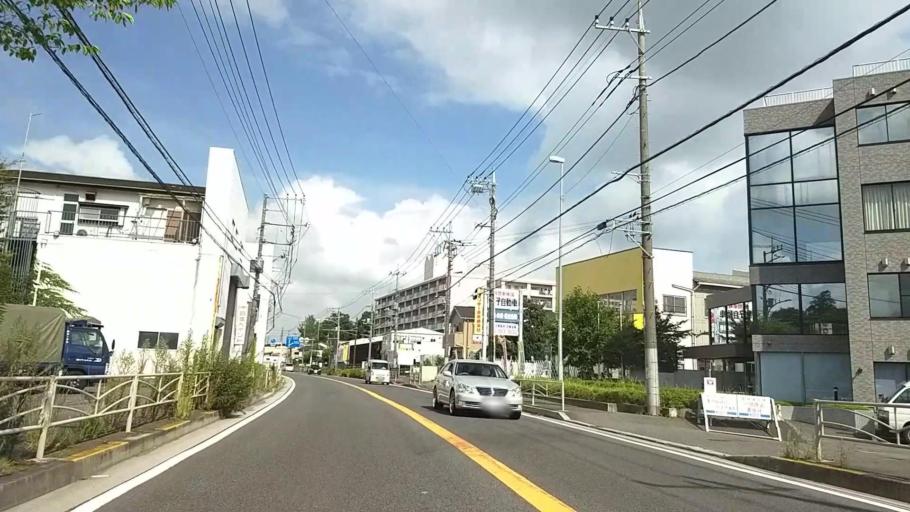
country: JP
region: Kanagawa
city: Minami-rinkan
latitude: 35.4927
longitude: 139.5114
